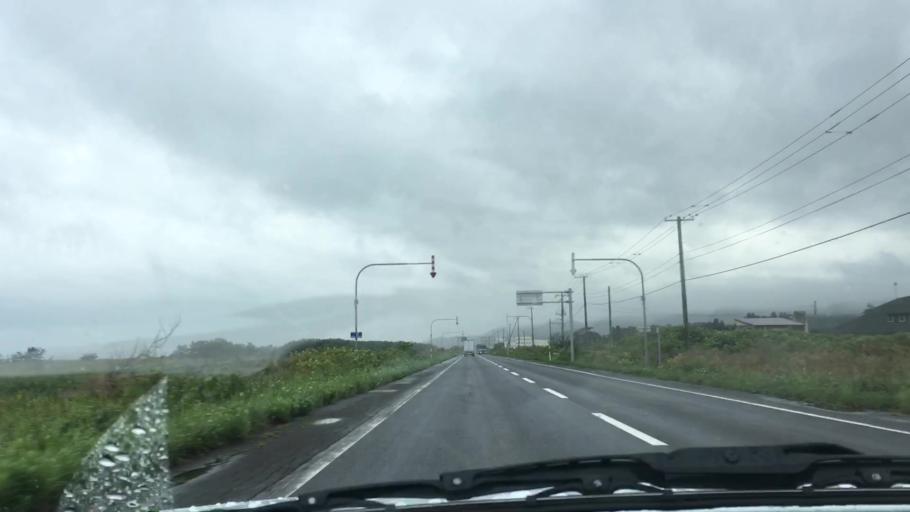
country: JP
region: Hokkaido
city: Niseko Town
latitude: 42.3952
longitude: 140.3005
